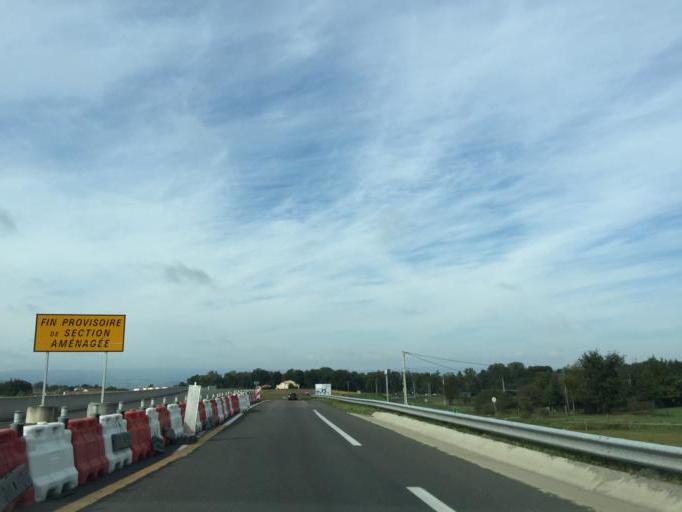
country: FR
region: Rhone-Alpes
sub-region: Departement de la Loire
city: Saint-Just-Saint-Rambert
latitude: 45.5156
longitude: 4.2331
